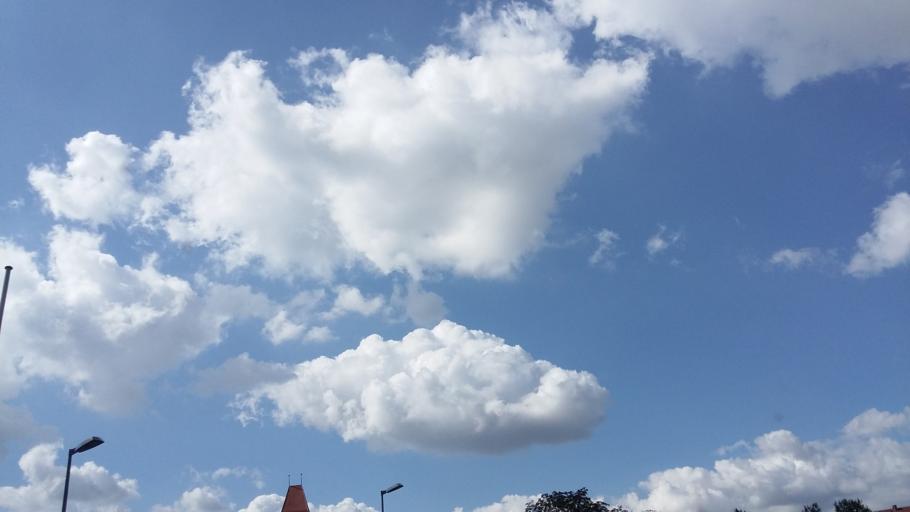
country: DE
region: Bavaria
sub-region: Swabia
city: Neu-Ulm
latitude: 48.3984
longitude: 10.0040
